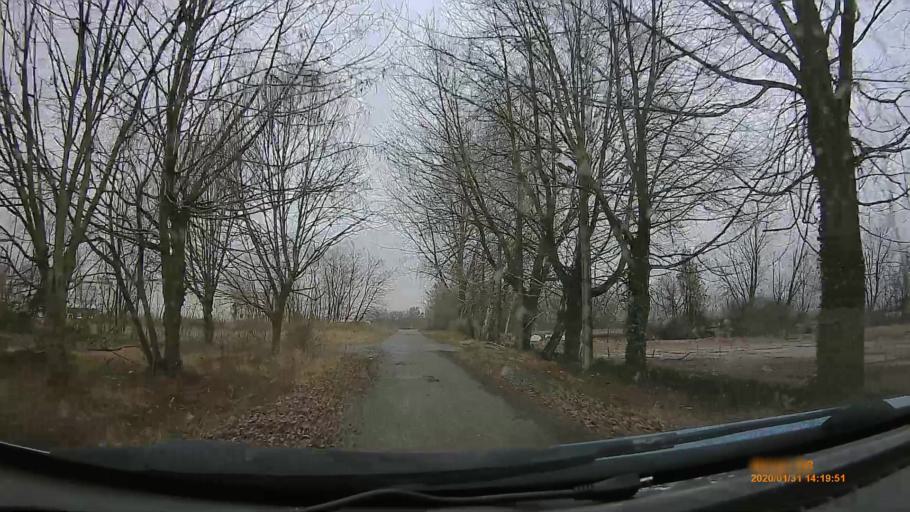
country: HU
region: Szabolcs-Szatmar-Bereg
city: Nyiregyhaza
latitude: 47.9547
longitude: 21.6787
